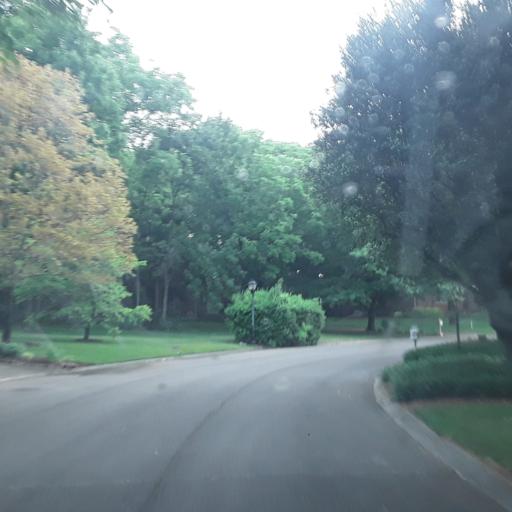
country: US
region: Tennessee
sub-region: Williamson County
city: Brentwood
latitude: 36.0467
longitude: -86.7711
